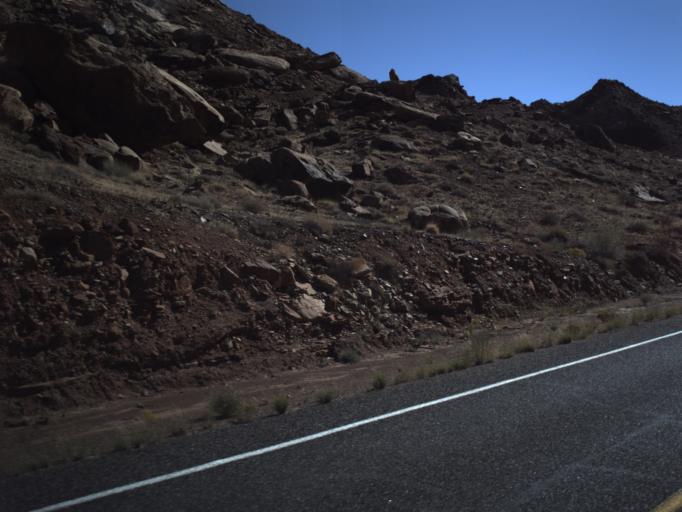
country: US
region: Utah
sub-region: San Juan County
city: Blanding
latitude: 37.8982
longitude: -110.4479
